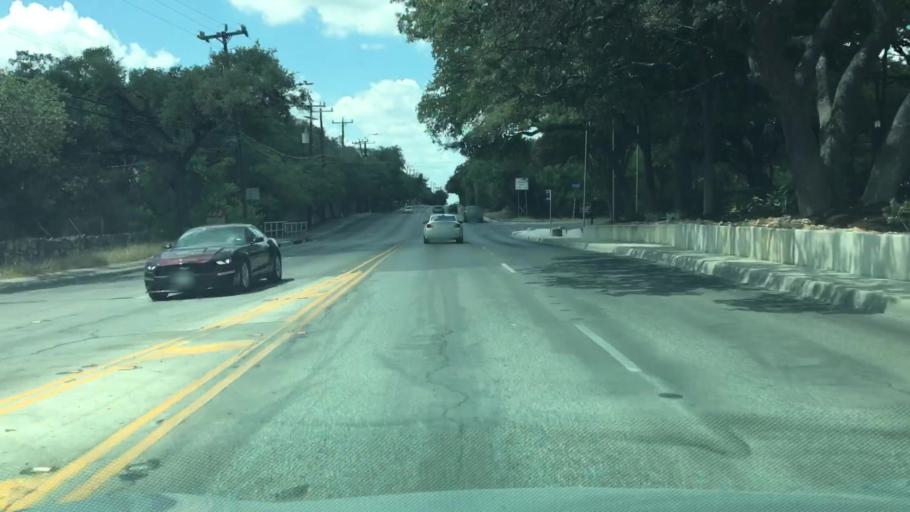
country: US
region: Texas
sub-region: Bexar County
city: Hollywood Park
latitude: 29.5579
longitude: -98.4735
